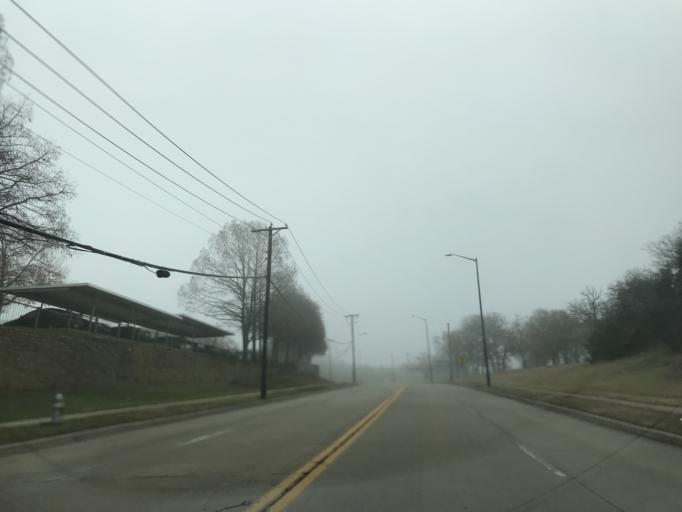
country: US
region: Texas
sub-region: Tarrant County
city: Arlington
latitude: 32.7740
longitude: -97.0870
